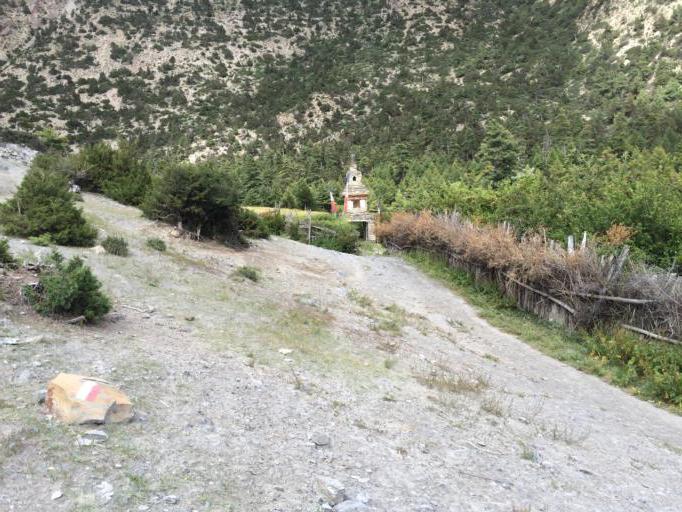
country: NP
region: Western Region
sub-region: Gandaki Zone
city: Nawal
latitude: 28.6604
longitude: 84.0851
